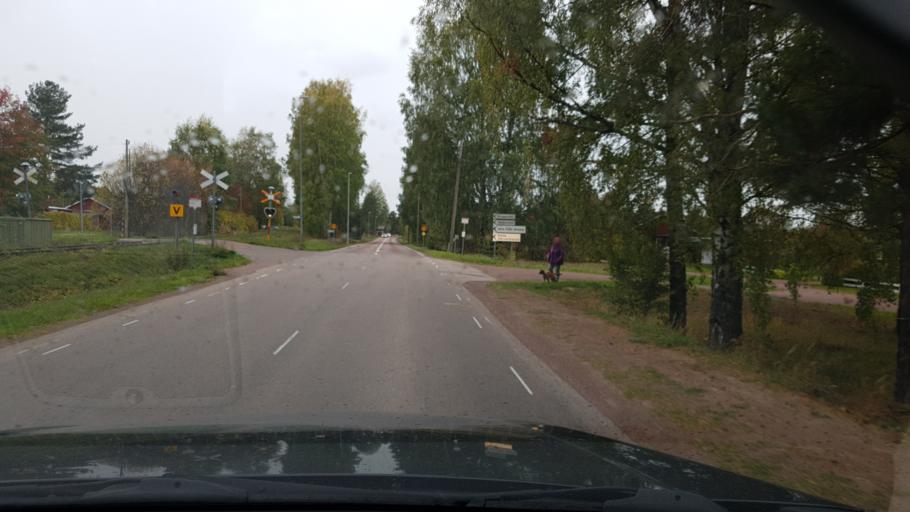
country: SE
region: Dalarna
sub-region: Mora Kommun
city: Mora
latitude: 61.0082
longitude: 14.5118
